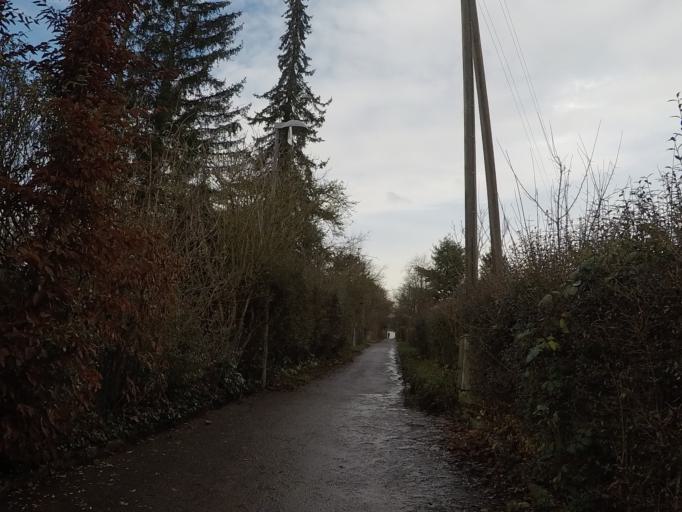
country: DE
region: Baden-Wuerttemberg
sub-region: Tuebingen Region
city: Ulm
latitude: 48.3902
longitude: 9.9554
